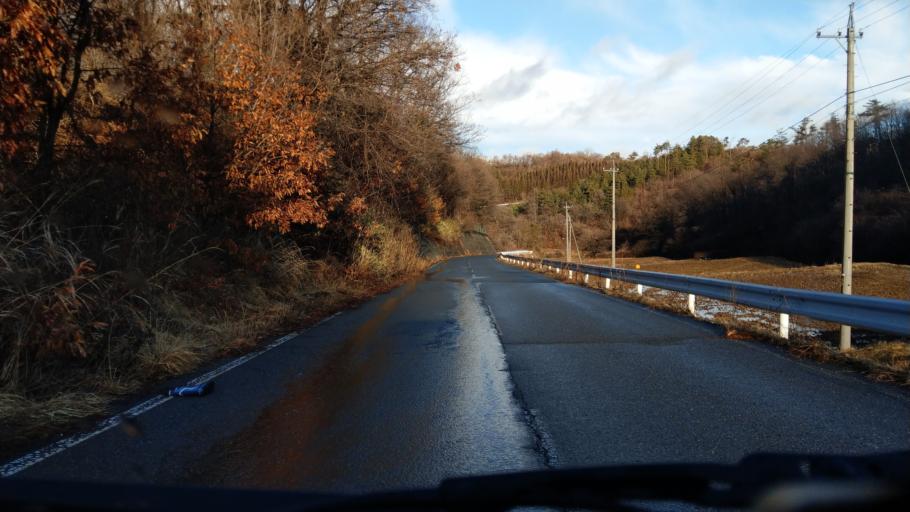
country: JP
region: Nagano
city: Kamimaruko
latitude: 36.2913
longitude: 138.3380
